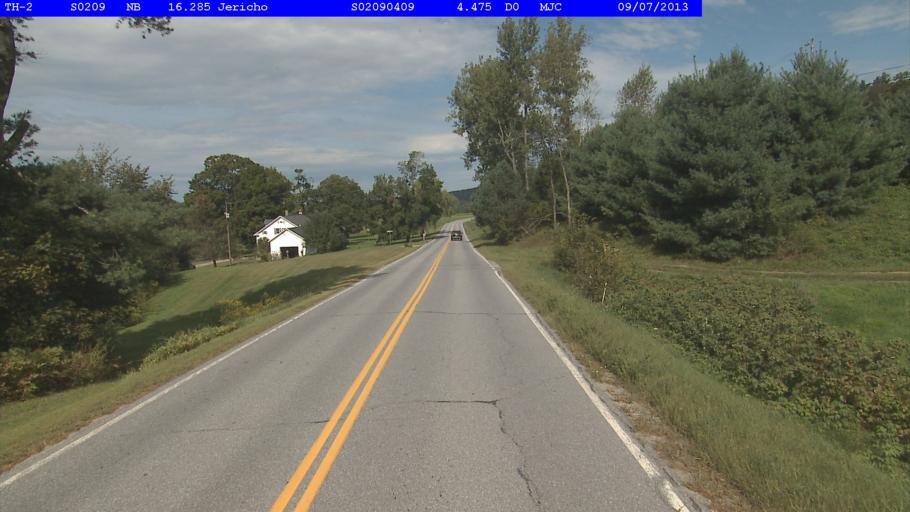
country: US
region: Vermont
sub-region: Chittenden County
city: Jericho
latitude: 44.4879
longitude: -72.9789
